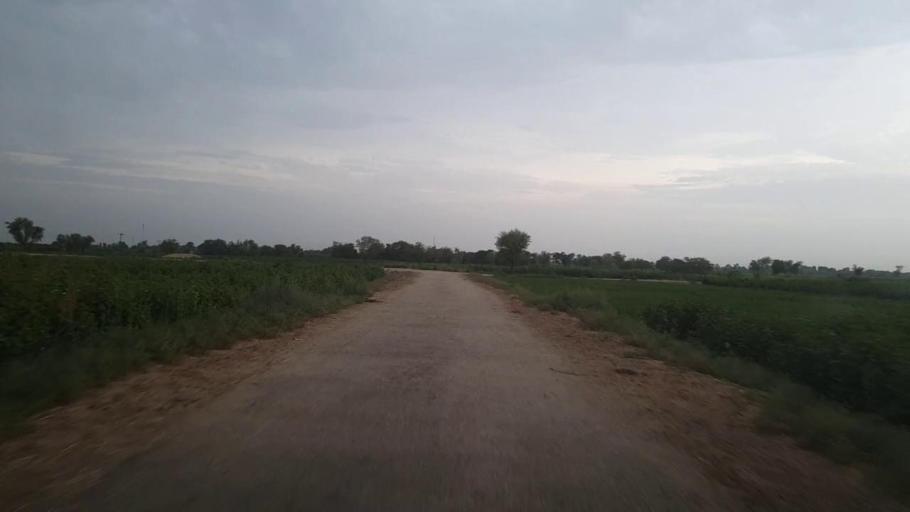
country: PK
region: Sindh
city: Karaundi
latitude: 27.0177
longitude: 68.3473
